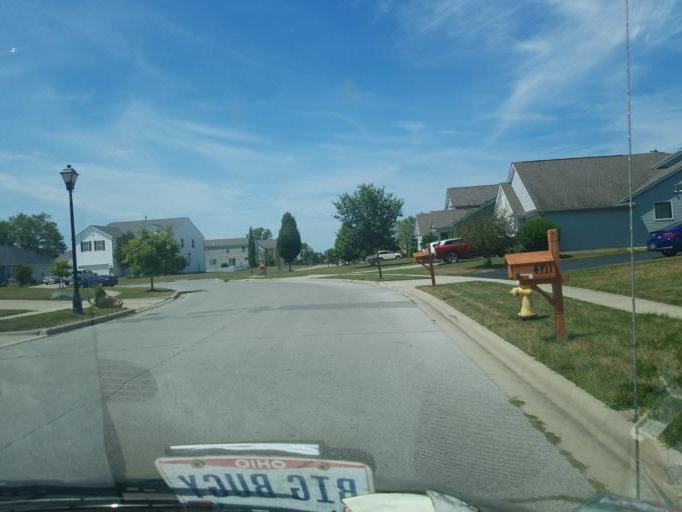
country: US
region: Ohio
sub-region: Franklin County
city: Grove City
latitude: 39.8655
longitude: -83.0907
